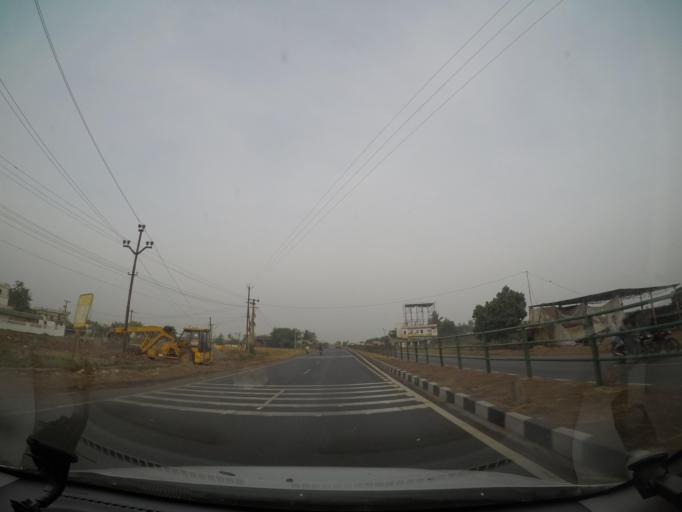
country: IN
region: Andhra Pradesh
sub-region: West Godavari
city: Eluru
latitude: 16.6327
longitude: 80.9571
